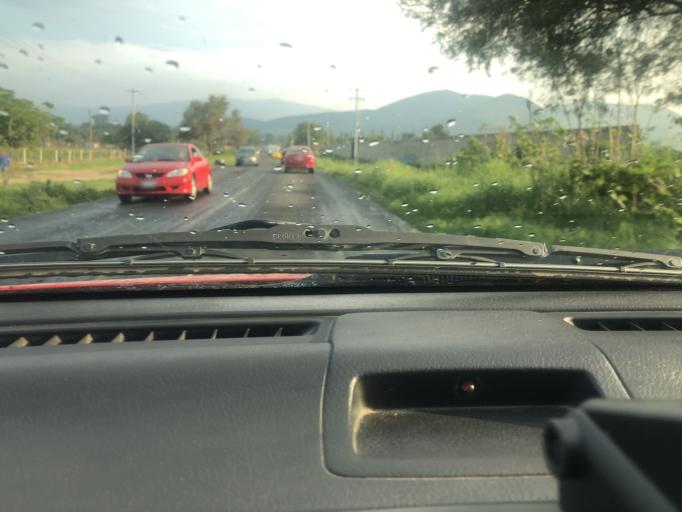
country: MX
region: Jalisco
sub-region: San Pedro Tlaquepaque
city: Santa Anita
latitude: 20.5486
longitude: -103.4205
